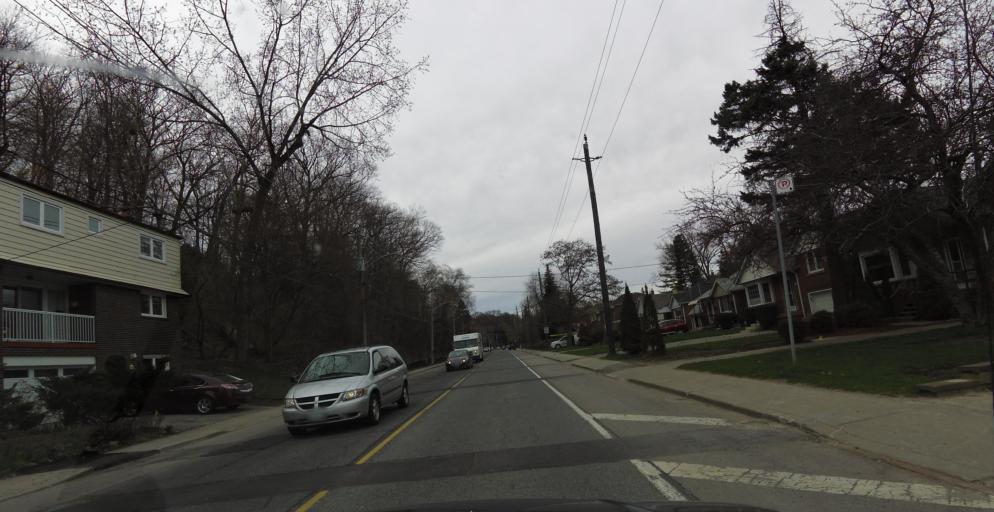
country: CA
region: Ontario
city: Toronto
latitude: 43.6410
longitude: -79.4788
